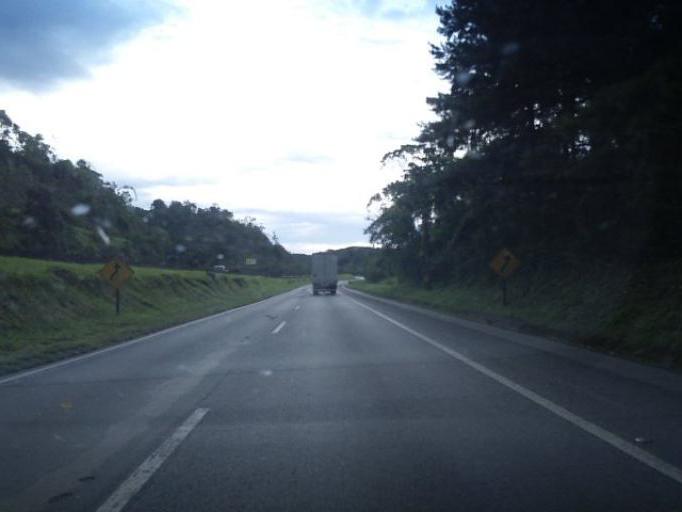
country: BR
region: Parana
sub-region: Antonina
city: Antonina
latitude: -25.0984
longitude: -48.6834
